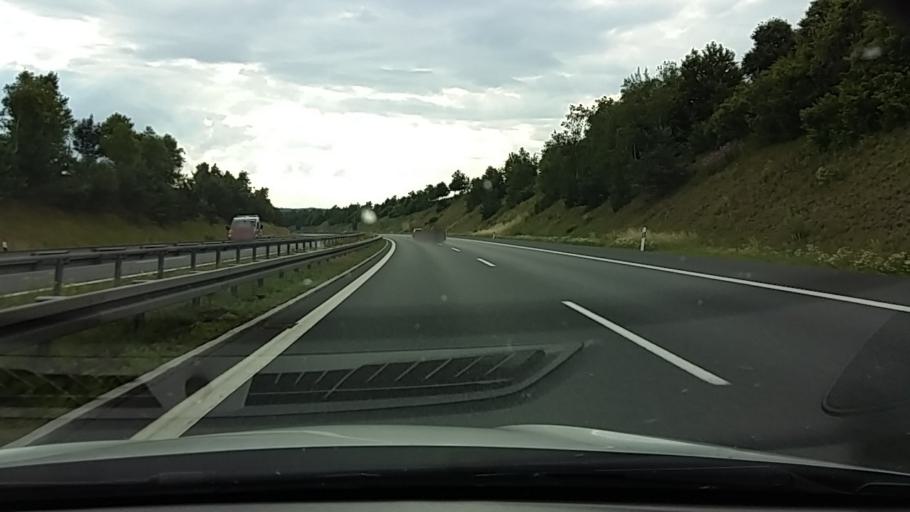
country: DE
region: Bavaria
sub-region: Upper Palatinate
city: Leuchtenberg
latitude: 49.5691
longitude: 12.2286
